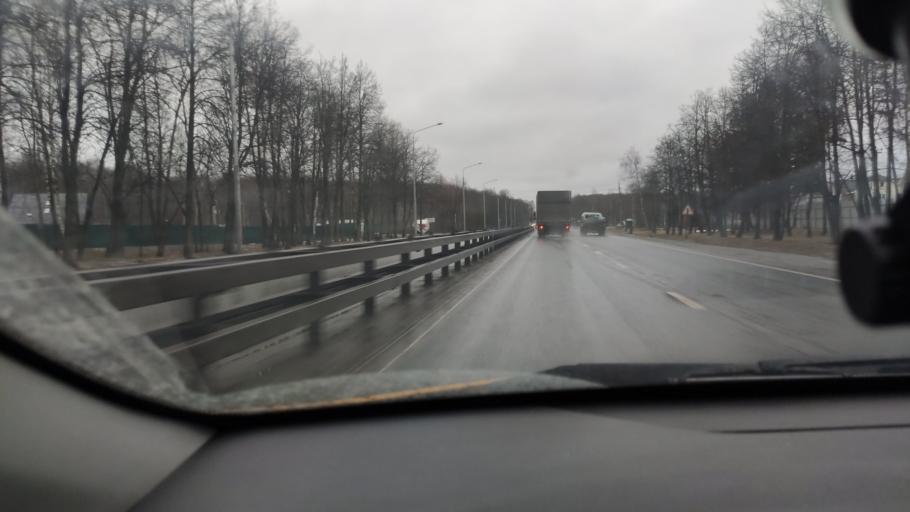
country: RU
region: Moskovskaya
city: Troitsk
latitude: 55.3551
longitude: 37.3468
